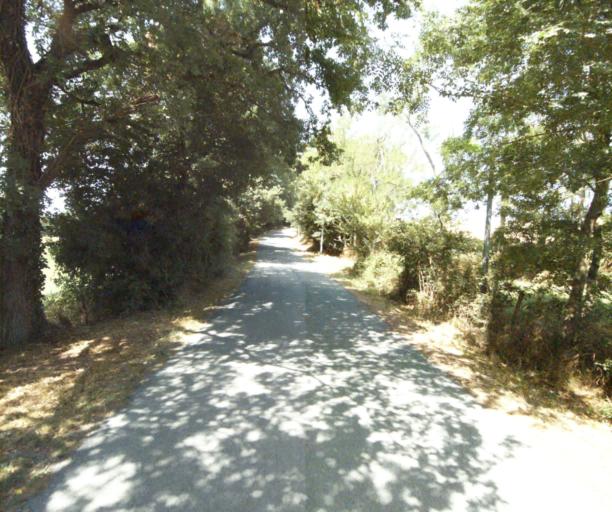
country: FR
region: Midi-Pyrenees
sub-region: Departement de la Haute-Garonne
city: Revel
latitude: 43.4952
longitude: 2.0213
